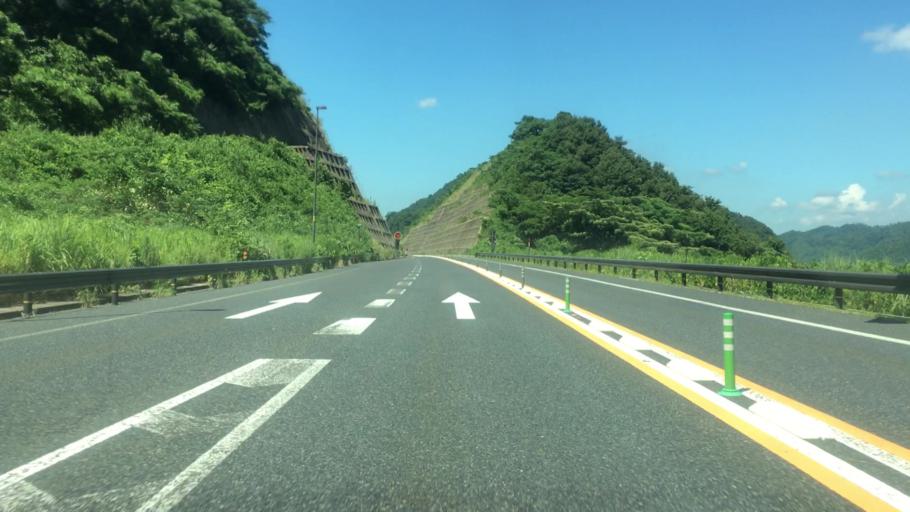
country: JP
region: Tottori
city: Tottori
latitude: 35.3573
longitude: 134.1980
